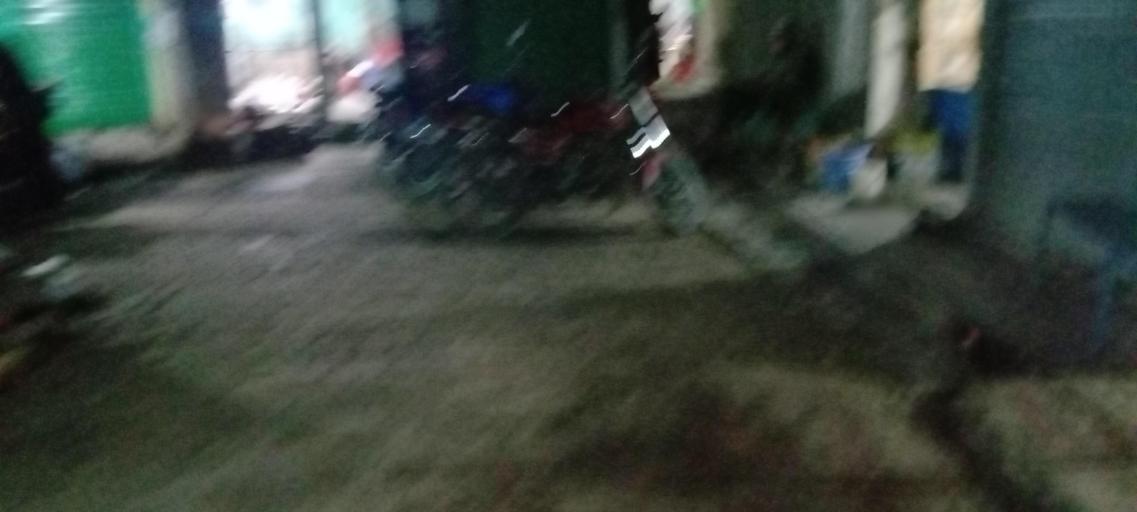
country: BD
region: Dhaka
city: Narayanganj
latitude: 23.6325
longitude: 90.4392
